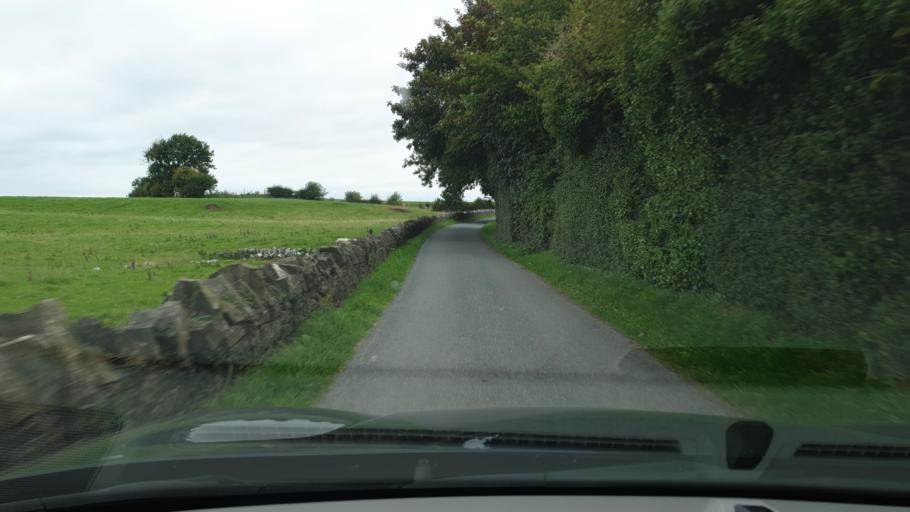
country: IE
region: Leinster
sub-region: An Mhi
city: Dunshaughlin
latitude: 53.4916
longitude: -6.5713
